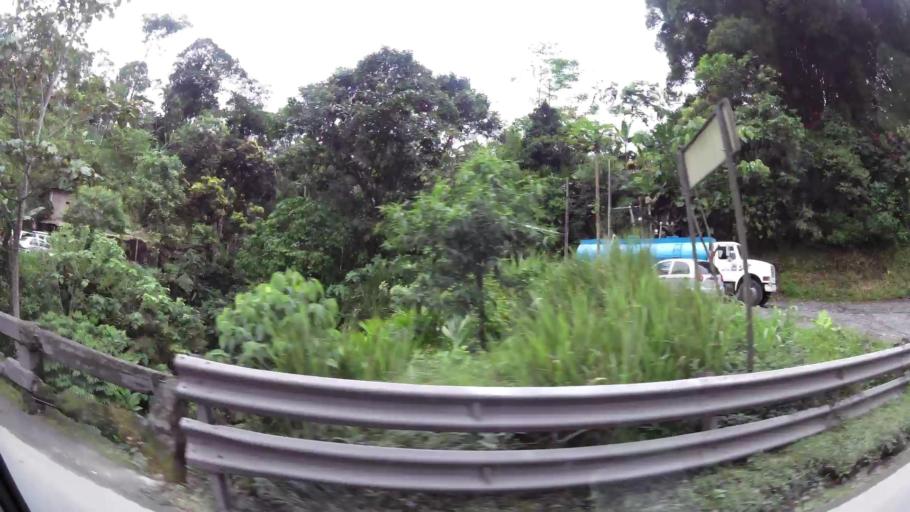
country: EC
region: Santo Domingo de los Tsachilas
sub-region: Canton Santo Domingo de los Colorados
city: Santo Domingo de los Colorados
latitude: -0.2697
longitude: -79.0931
